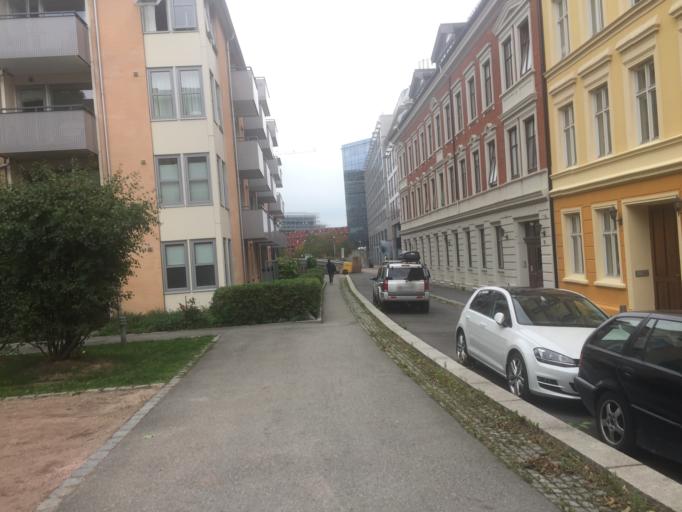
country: NO
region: Oslo
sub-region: Oslo
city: Oslo
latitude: 59.9117
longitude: 10.7224
